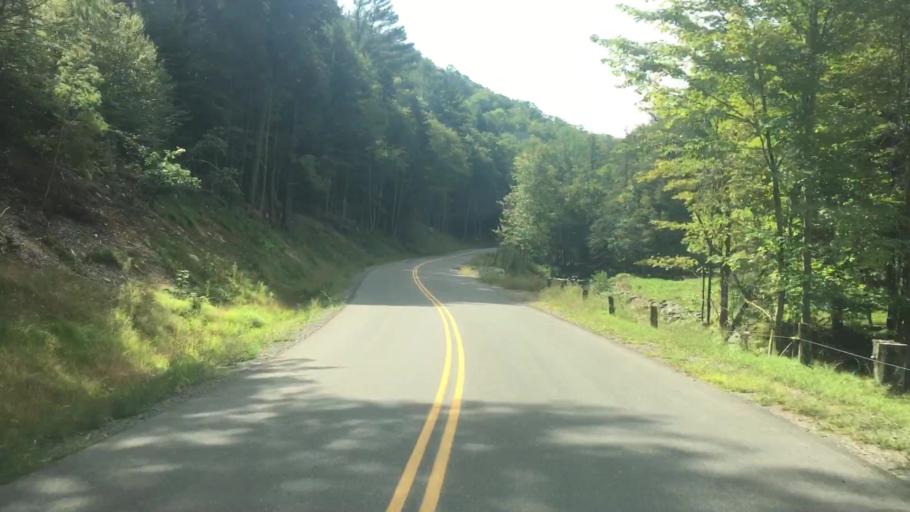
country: US
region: Massachusetts
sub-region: Franklin County
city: Colrain
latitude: 42.7785
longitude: -72.7684
